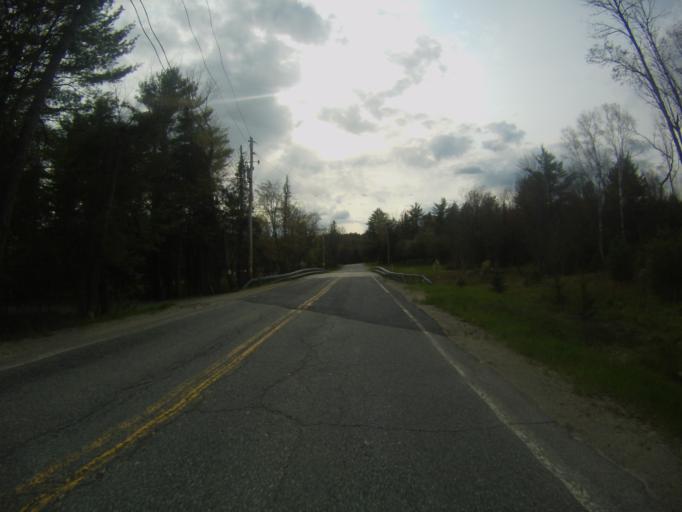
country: US
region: New York
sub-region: Warren County
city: Warrensburg
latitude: 43.8399
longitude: -73.8528
